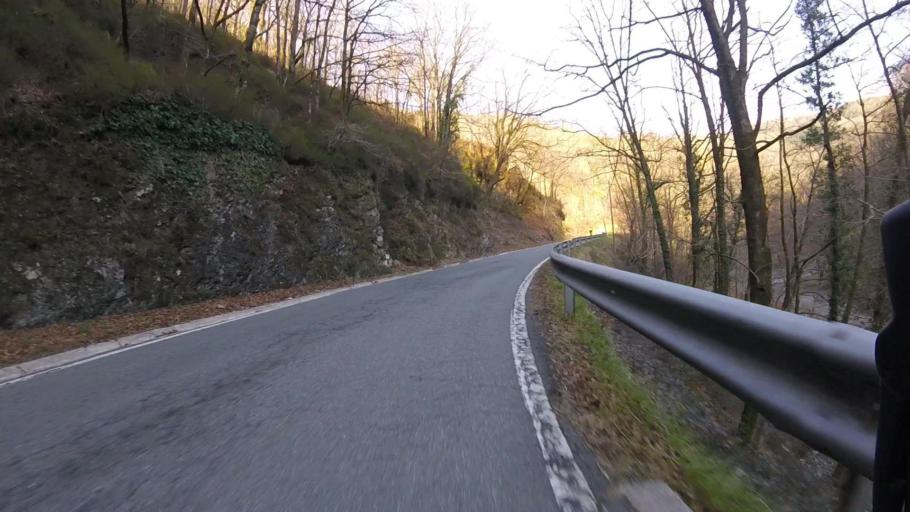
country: ES
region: Navarre
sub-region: Provincia de Navarra
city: Arano
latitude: 43.2086
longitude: -1.8659
